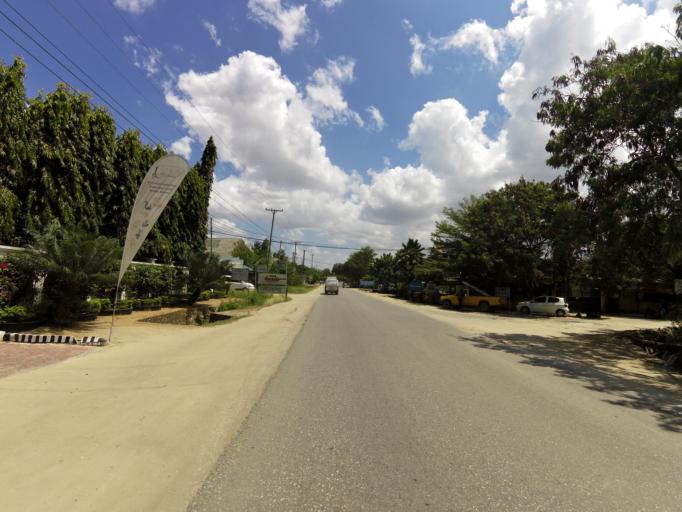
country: TZ
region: Dar es Salaam
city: Magomeni
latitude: -6.7630
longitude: 39.2501
